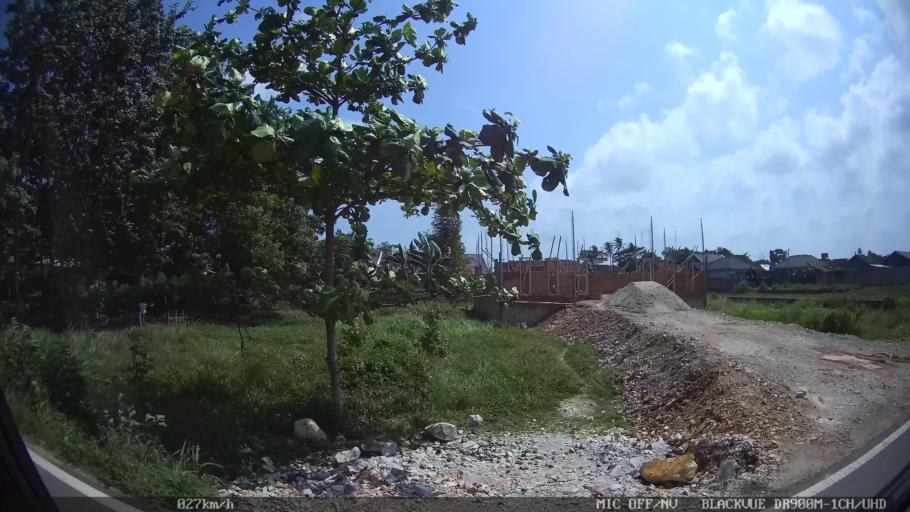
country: ID
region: Lampung
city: Kedaton
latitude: -5.3477
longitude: 105.2783
